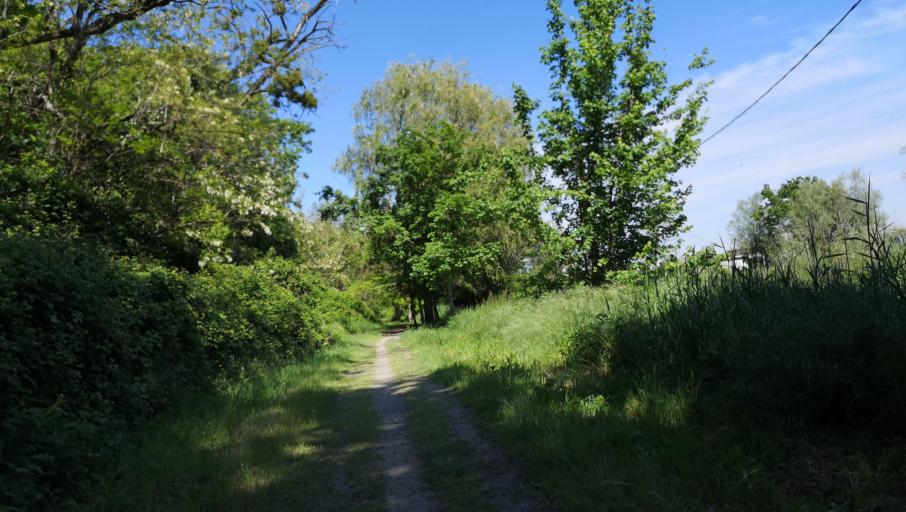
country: FR
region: Midi-Pyrenees
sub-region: Departement de la Haute-Garonne
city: Beauzelle
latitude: 43.6561
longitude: 1.3908
